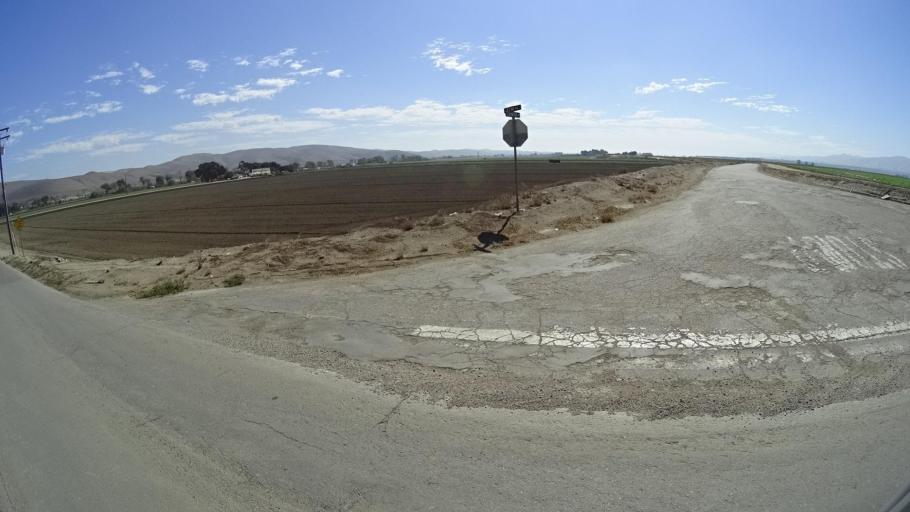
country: US
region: California
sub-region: Monterey County
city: Greenfield
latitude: 36.3340
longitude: -121.2124
